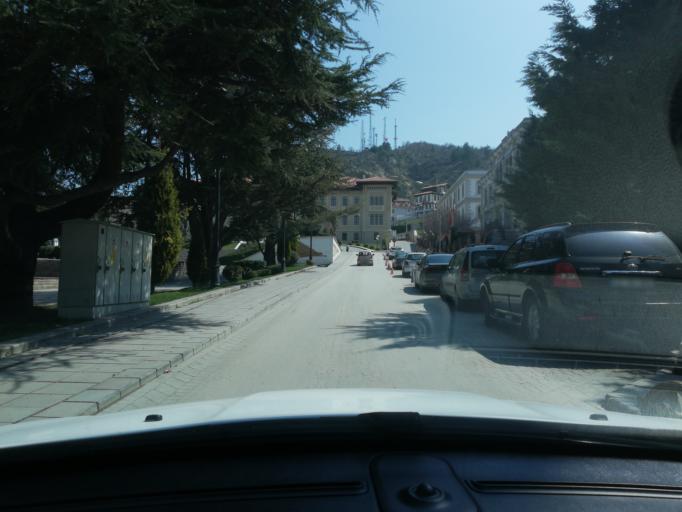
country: TR
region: Kastamonu
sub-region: Cide
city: Kastamonu
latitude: 41.3763
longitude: 33.7771
